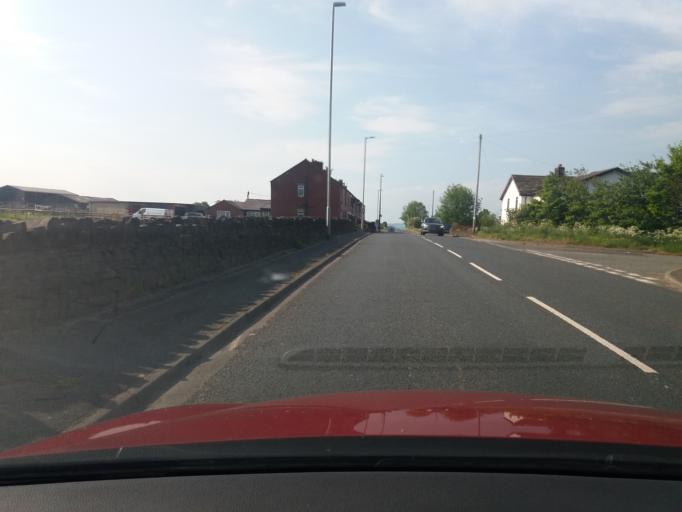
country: GB
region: England
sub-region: Blackburn with Darwen
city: Blackburn
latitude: 53.7067
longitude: -2.5523
